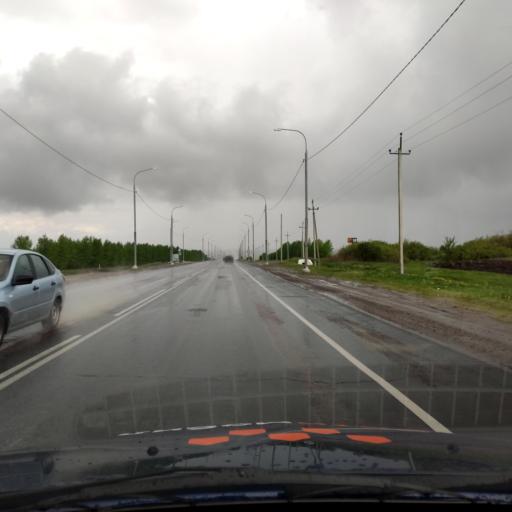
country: RU
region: Voronezj
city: Devitsa
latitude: 51.6321
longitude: 38.9734
